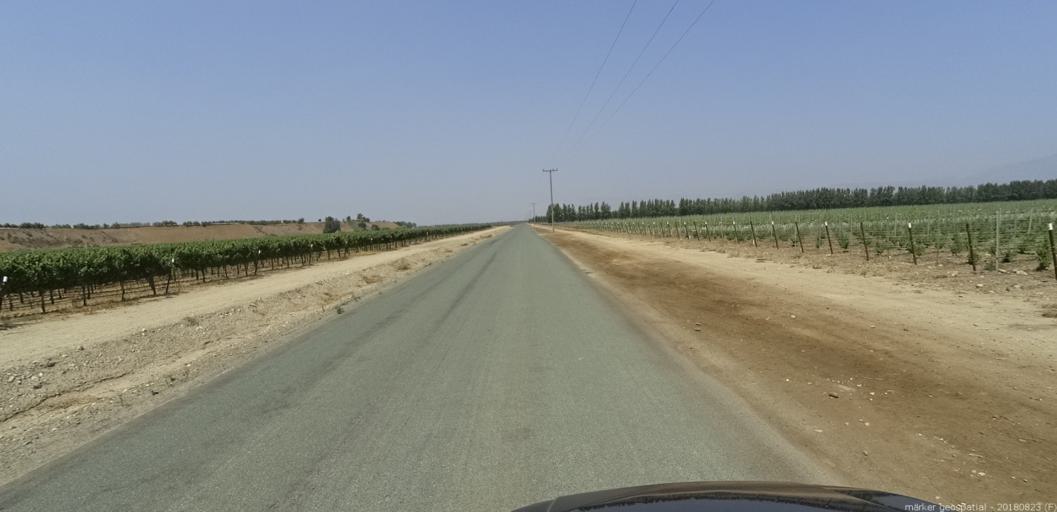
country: US
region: California
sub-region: Monterey County
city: Greenfield
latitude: 36.3460
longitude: -121.2988
